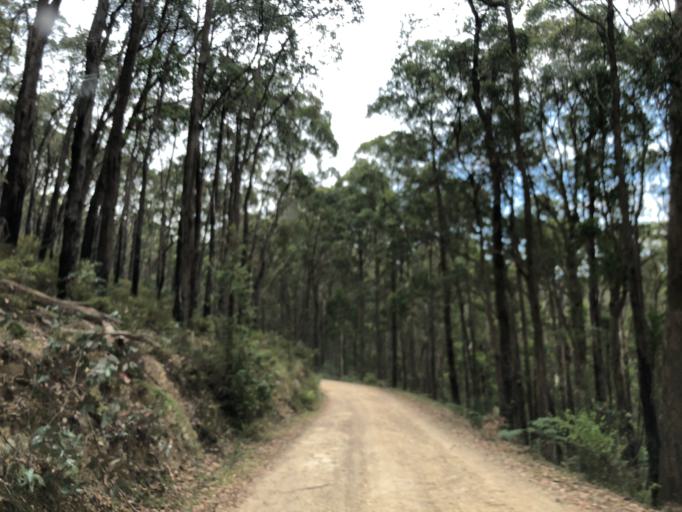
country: AU
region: Victoria
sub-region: Moorabool
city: Bacchus Marsh
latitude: -37.4596
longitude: 144.2714
